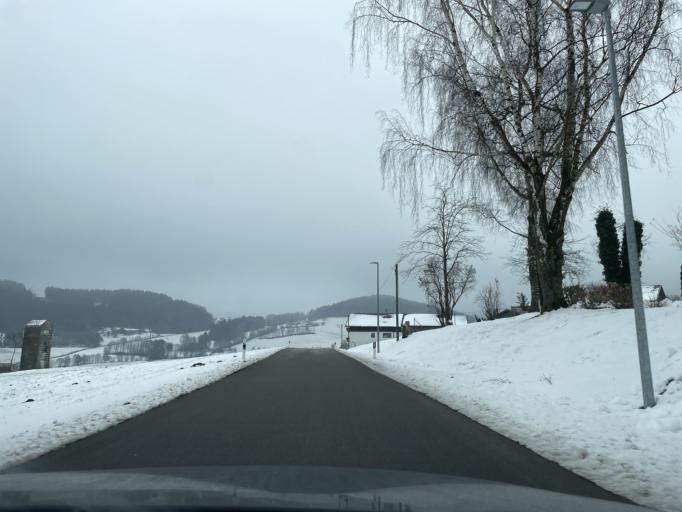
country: DE
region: Bavaria
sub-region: Lower Bavaria
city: Kollnburg
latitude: 49.0167
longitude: 12.8800
